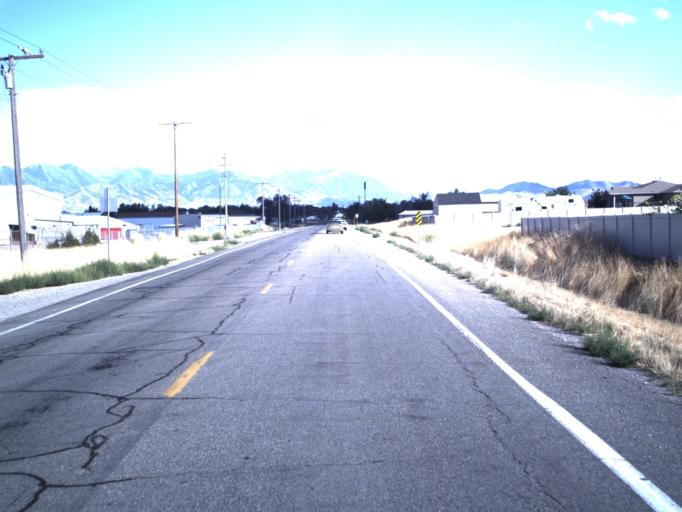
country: US
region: Utah
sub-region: Tooele County
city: Grantsville
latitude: 40.6055
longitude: -112.4879
